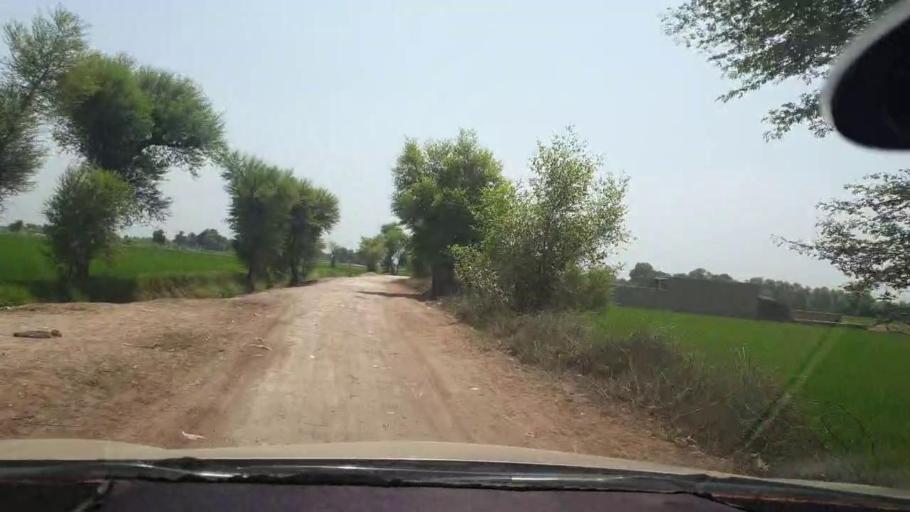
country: PK
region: Sindh
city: Kambar
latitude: 27.6699
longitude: 67.9430
